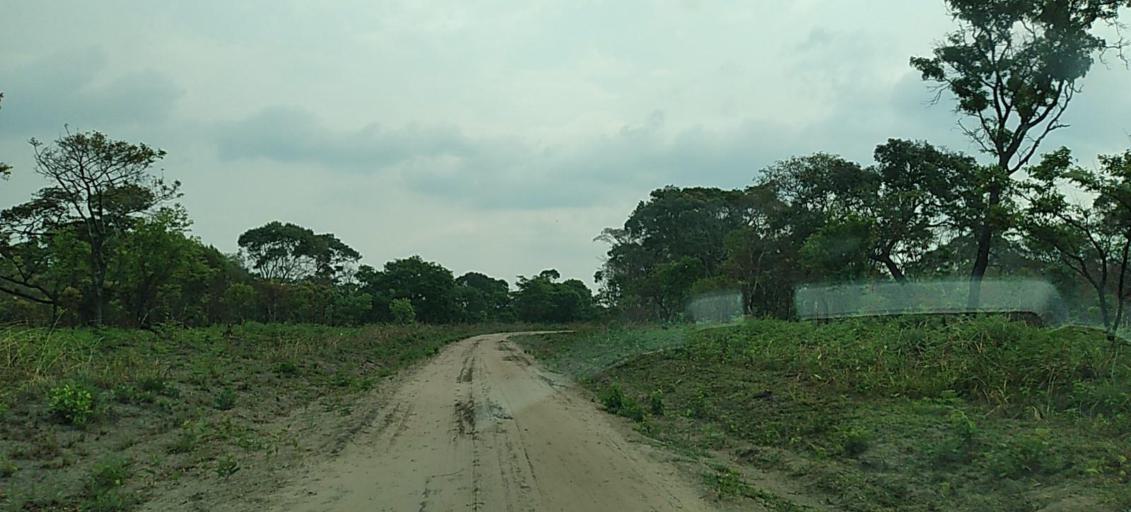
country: ZM
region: North-Western
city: Mwinilunga
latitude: -11.4061
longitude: 24.6285
